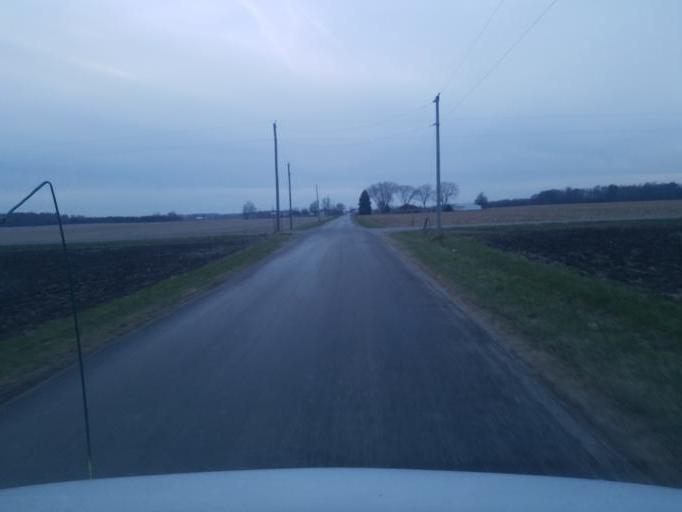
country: US
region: Indiana
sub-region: Adams County
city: Decatur
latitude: 40.7879
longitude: -84.9948
